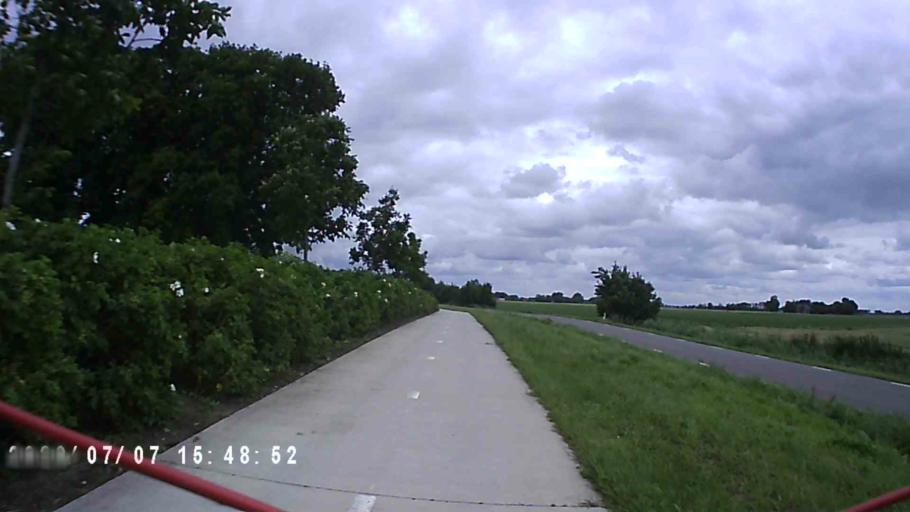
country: NL
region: Groningen
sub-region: Gemeente Winsum
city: Winsum
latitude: 53.3645
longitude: 6.4900
